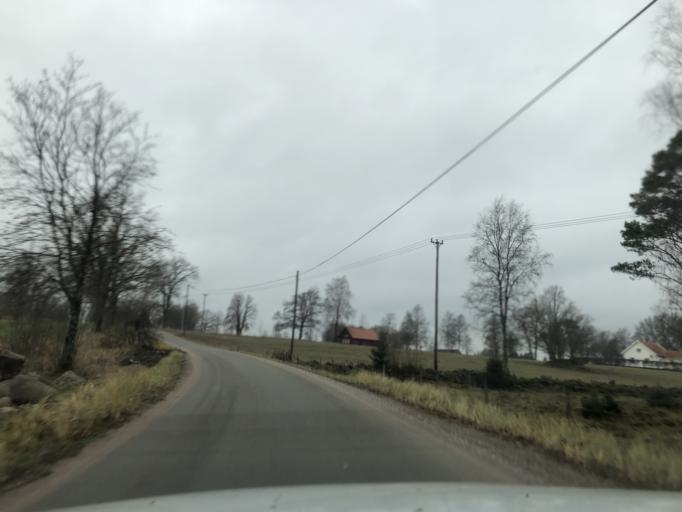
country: SE
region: Vaestra Goetaland
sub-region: Ulricehamns Kommun
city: Ulricehamn
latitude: 57.8616
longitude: 13.5937
